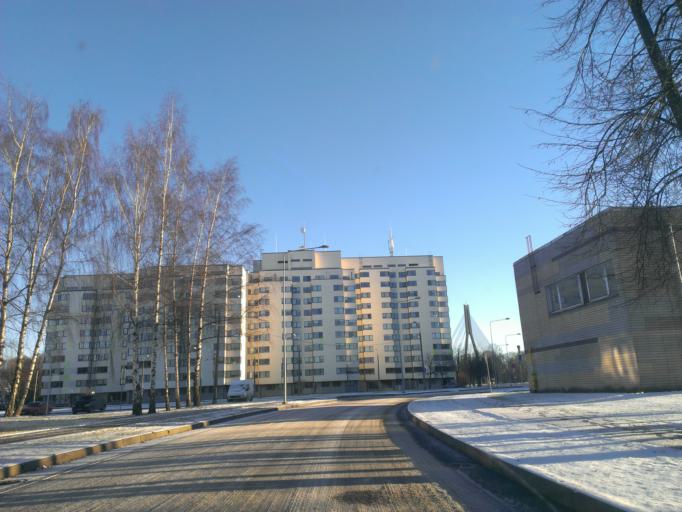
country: LV
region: Riga
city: Riga
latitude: 56.9506
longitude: 24.0802
